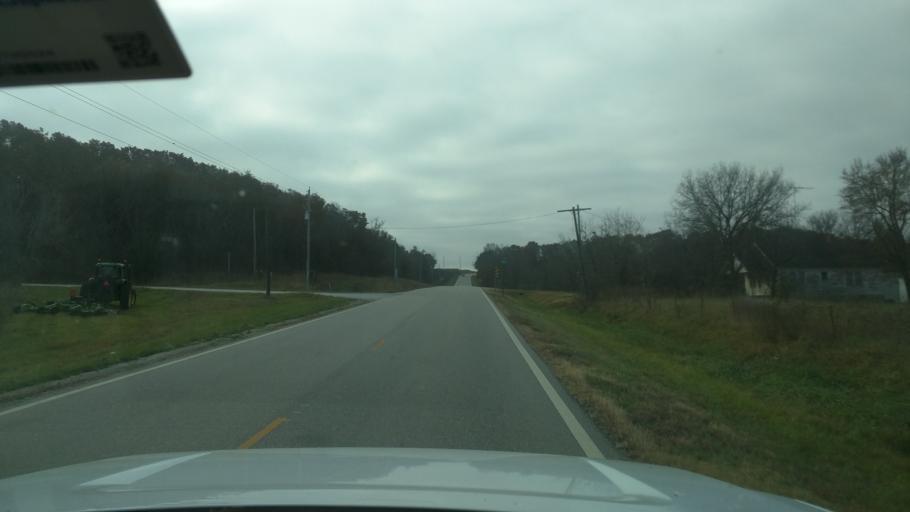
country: US
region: Kansas
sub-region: Greenwood County
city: Eureka
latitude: 37.7043
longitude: -96.2229
